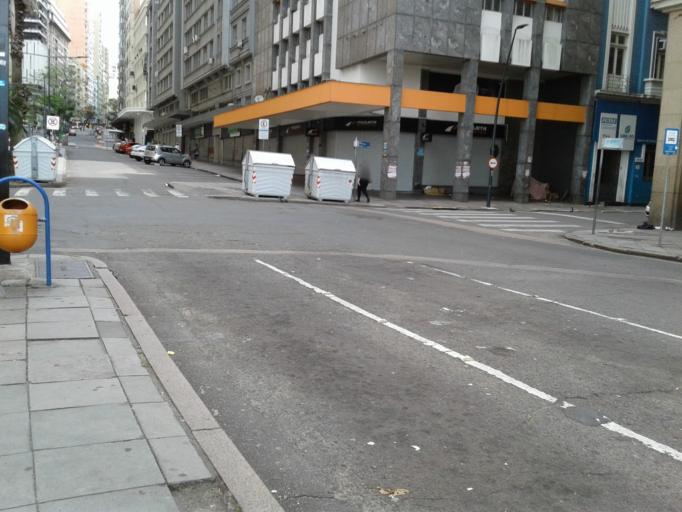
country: BR
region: Rio Grande do Sul
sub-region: Porto Alegre
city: Porto Alegre
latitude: -30.0288
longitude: -51.2280
